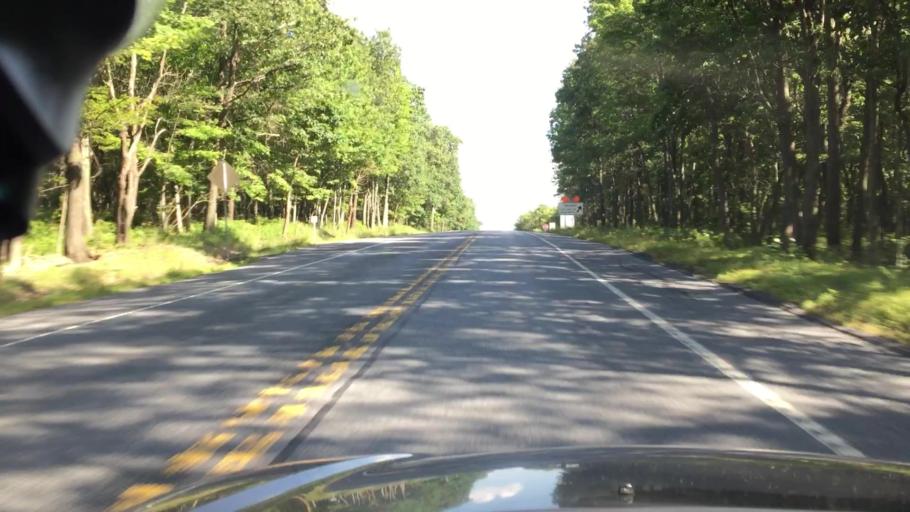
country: US
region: Pennsylvania
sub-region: Carbon County
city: Nesquehoning
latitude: 40.8903
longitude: -75.8047
